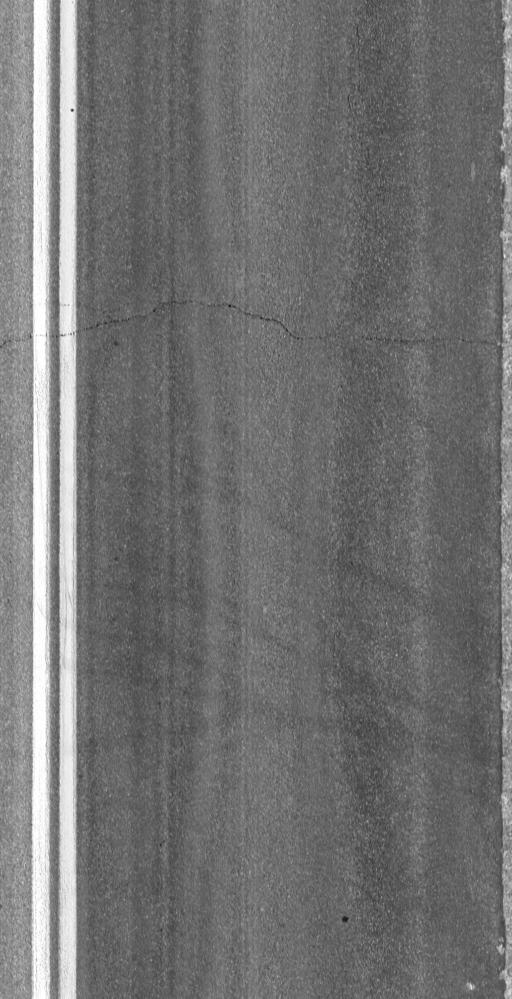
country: US
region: Vermont
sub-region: Chittenden County
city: Hinesburg
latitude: 44.3604
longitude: -73.2220
